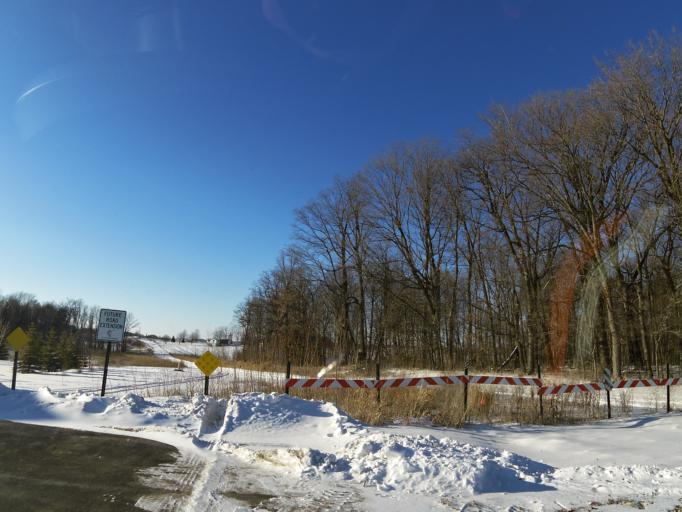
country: US
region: Minnesota
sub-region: Le Sueur County
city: New Prague
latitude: 44.5509
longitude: -93.6000
